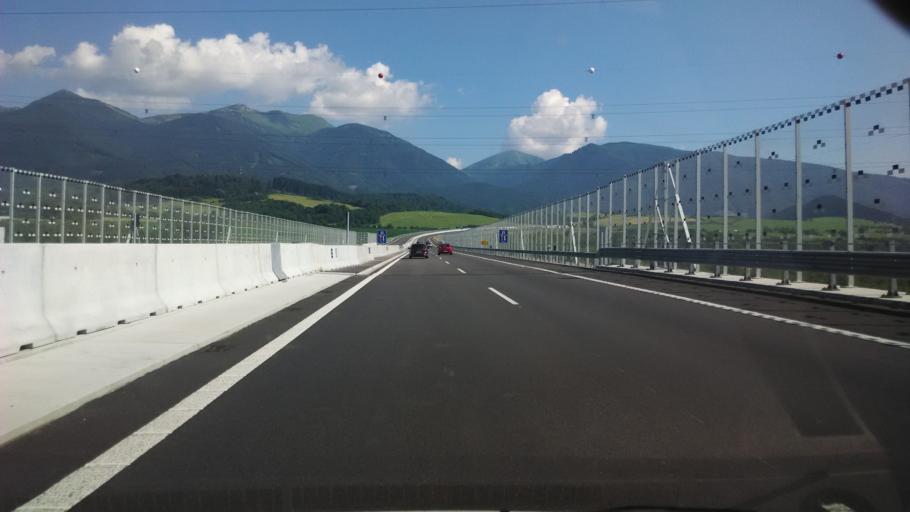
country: SK
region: Zilinsky
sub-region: Okres Zilina
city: Terchova
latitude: 49.1213
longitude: 19.0671
